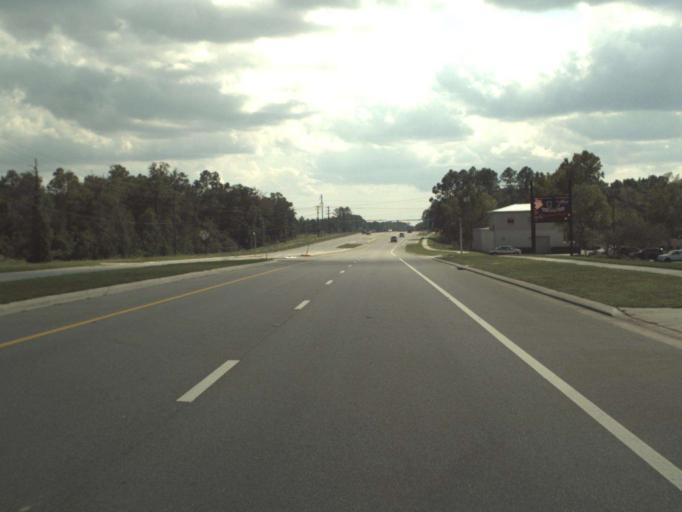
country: US
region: Florida
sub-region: Bay County
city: Laguna Beach
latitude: 30.4475
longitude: -85.8741
